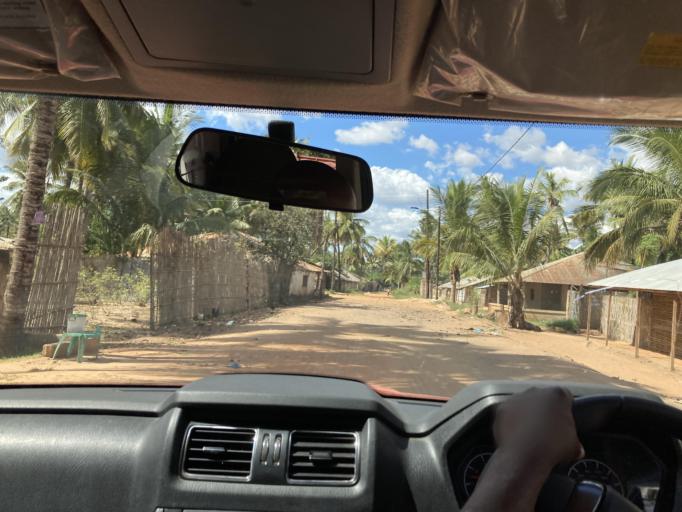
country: MZ
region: Cabo Delgado
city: Montepuez
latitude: -13.1341
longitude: 39.0057
